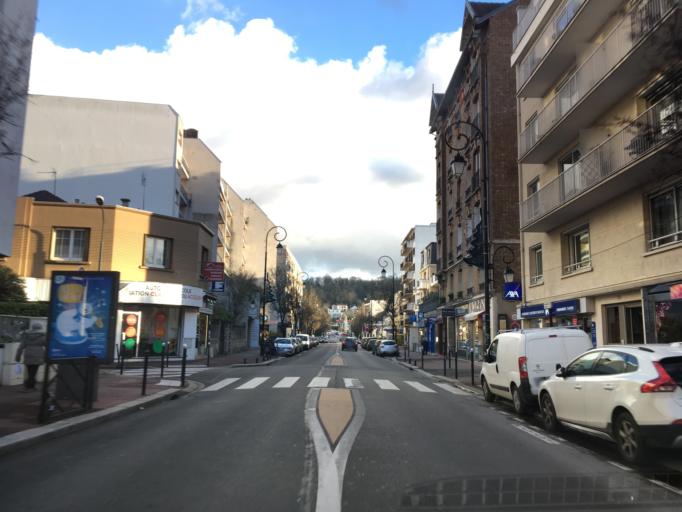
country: FR
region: Ile-de-France
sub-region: Departement du Val-de-Marne
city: Chennevieres-sur-Marne
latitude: 48.7924
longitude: 2.5174
